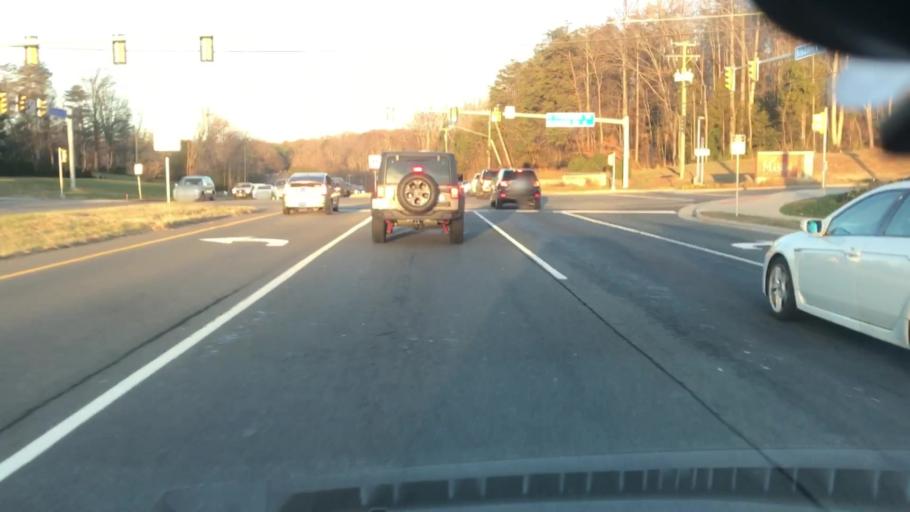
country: US
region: Virginia
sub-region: City of Fairfax
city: Fairfax
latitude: 38.8306
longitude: -77.3275
